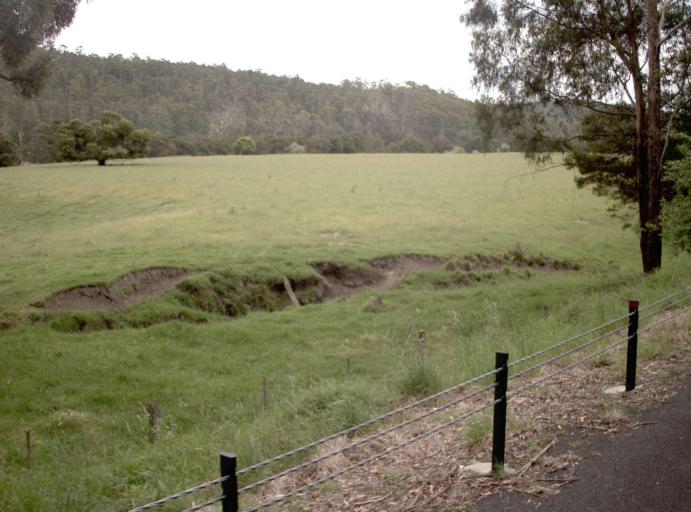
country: AU
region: New South Wales
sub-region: Bombala
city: Bombala
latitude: -37.4445
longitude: 149.1943
